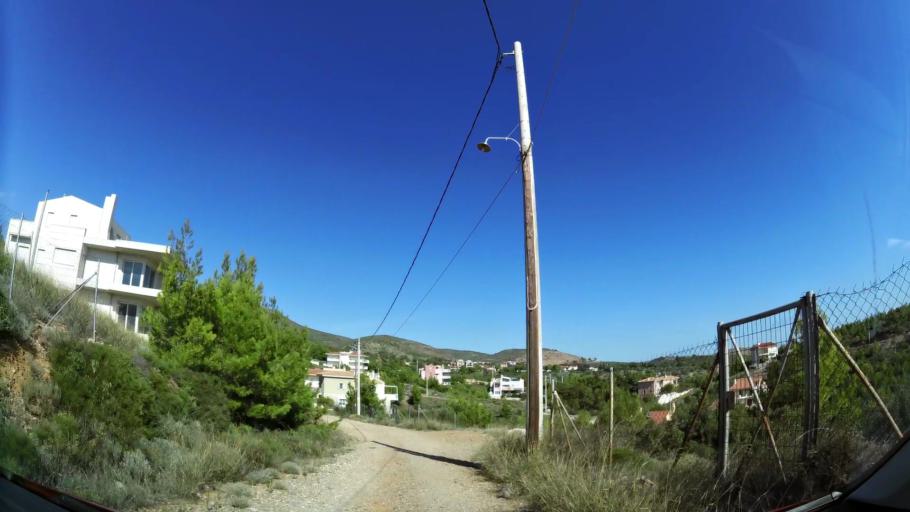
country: GR
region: Attica
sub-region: Nomarchia Anatolikis Attikis
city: Dioni
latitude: 38.0340
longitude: 23.9401
